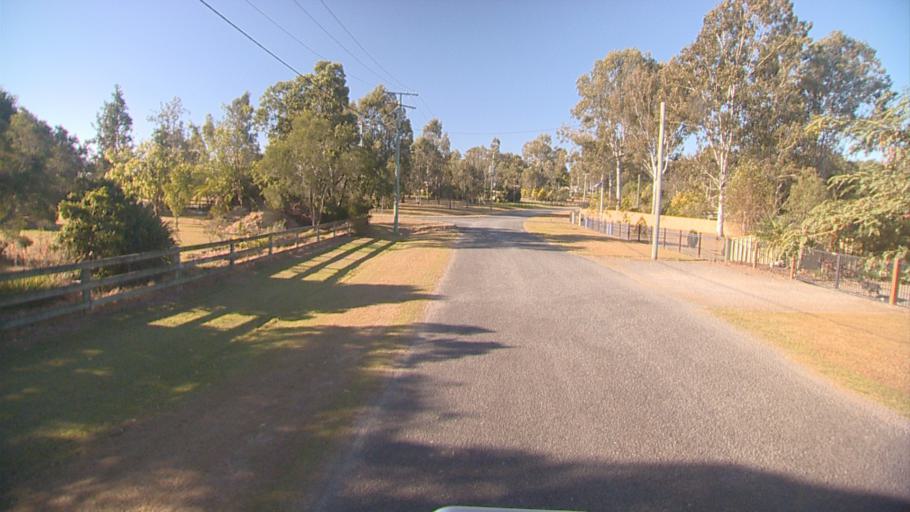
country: AU
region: Queensland
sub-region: Logan
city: Cedar Vale
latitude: -27.8290
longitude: 153.0199
